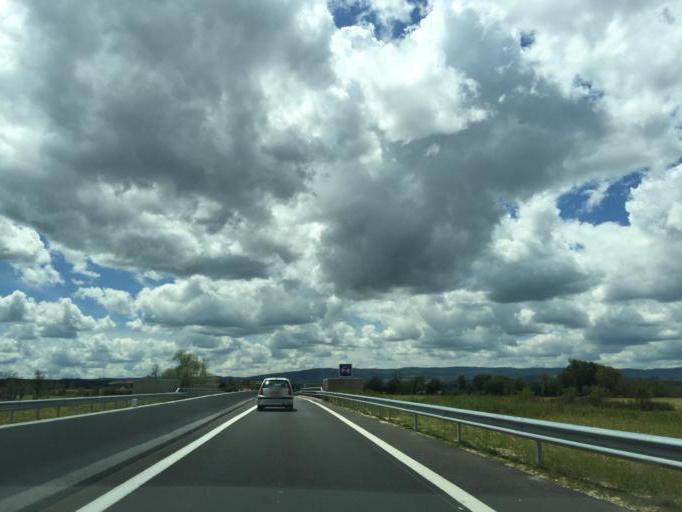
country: FR
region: Rhone-Alpes
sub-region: Departement de la Loire
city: Sury-le-Comtal
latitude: 45.5129
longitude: 4.1938
